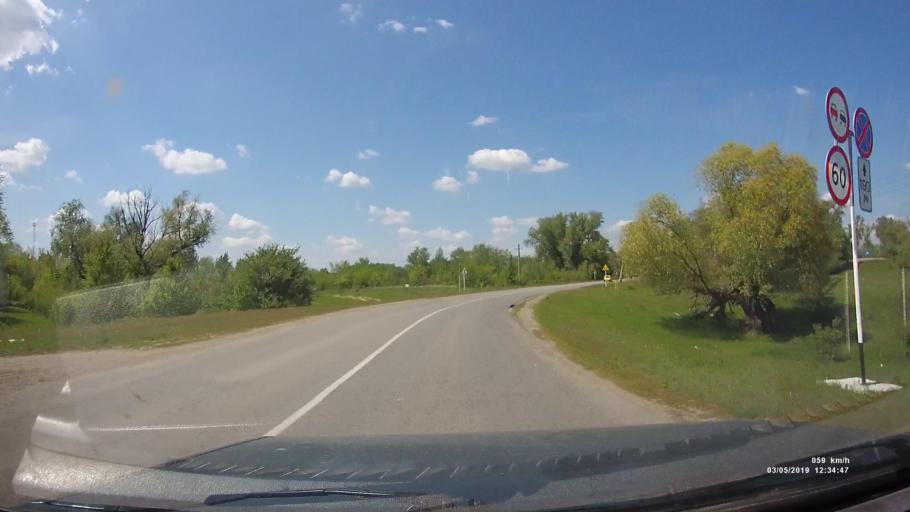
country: RU
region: Rostov
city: Semikarakorsk
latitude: 47.5230
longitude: 40.7664
